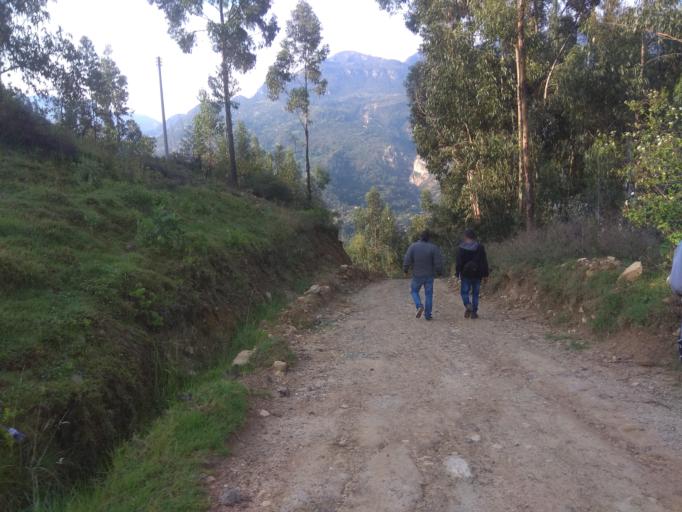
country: CO
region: Boyaca
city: Socha Viejo
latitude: 5.9888
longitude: -72.7019
